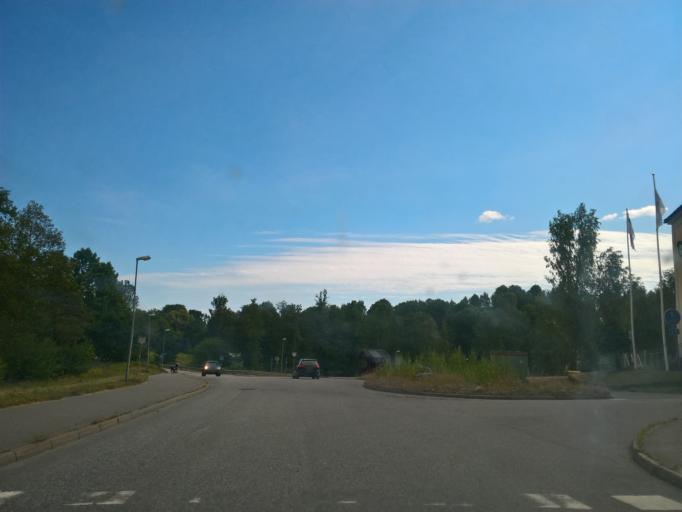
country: SE
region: OEstergoetland
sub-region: Finspangs Kommun
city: Finspang
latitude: 58.7353
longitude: 15.8227
